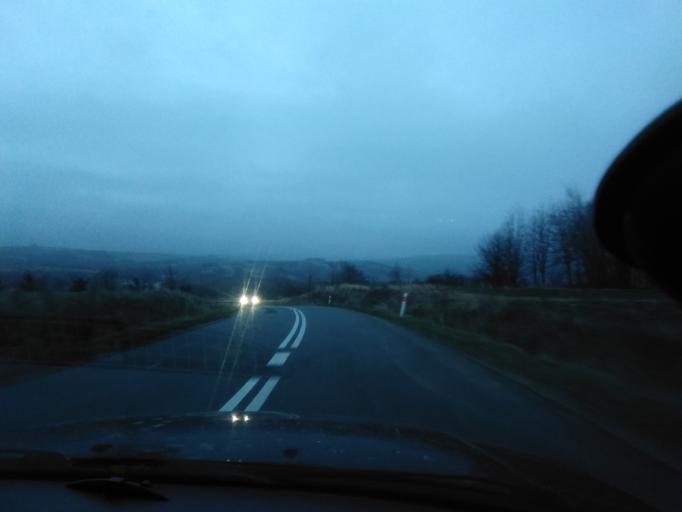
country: PL
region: Subcarpathian Voivodeship
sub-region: Powiat jaroslawski
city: Jodlowka
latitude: 49.8824
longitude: 22.4658
